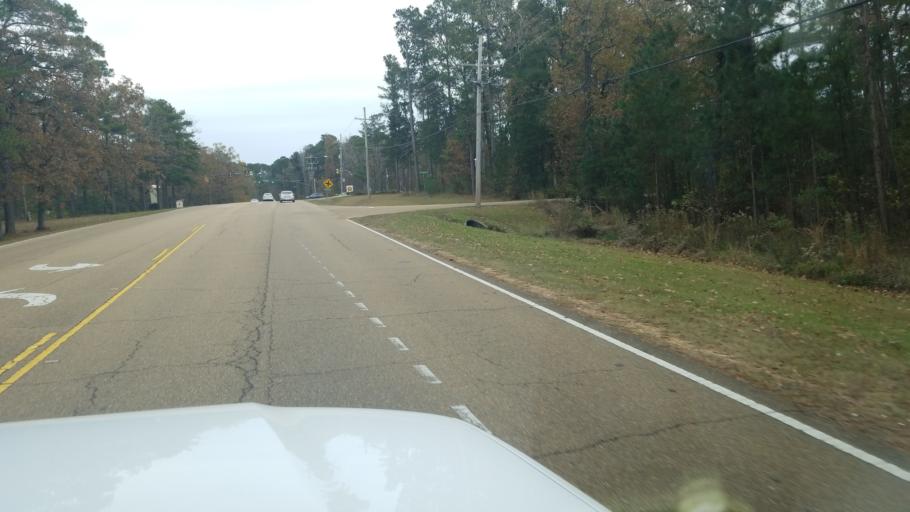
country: US
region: Mississippi
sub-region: Rankin County
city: Brandon
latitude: 32.3733
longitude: -90.0189
